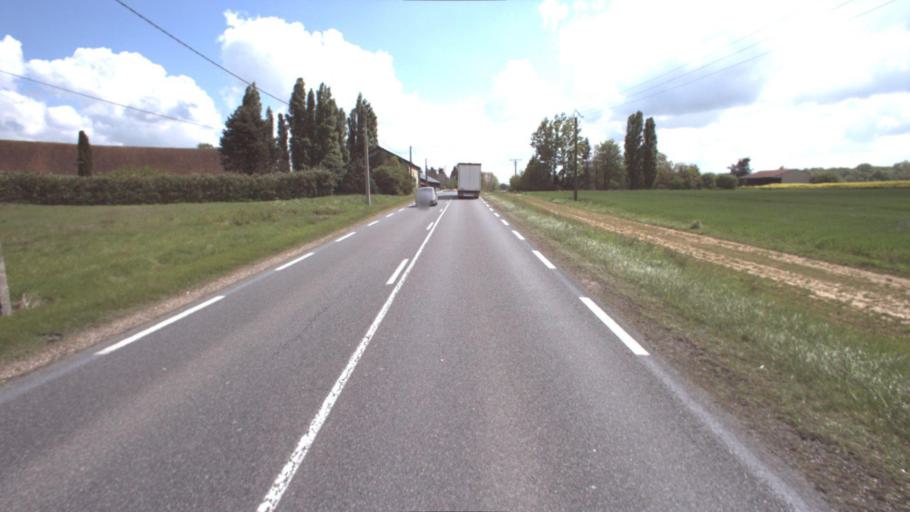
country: FR
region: Ile-de-France
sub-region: Departement de Seine-et-Marne
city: Jouy-le-Chatel
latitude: 48.6924
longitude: 3.1686
